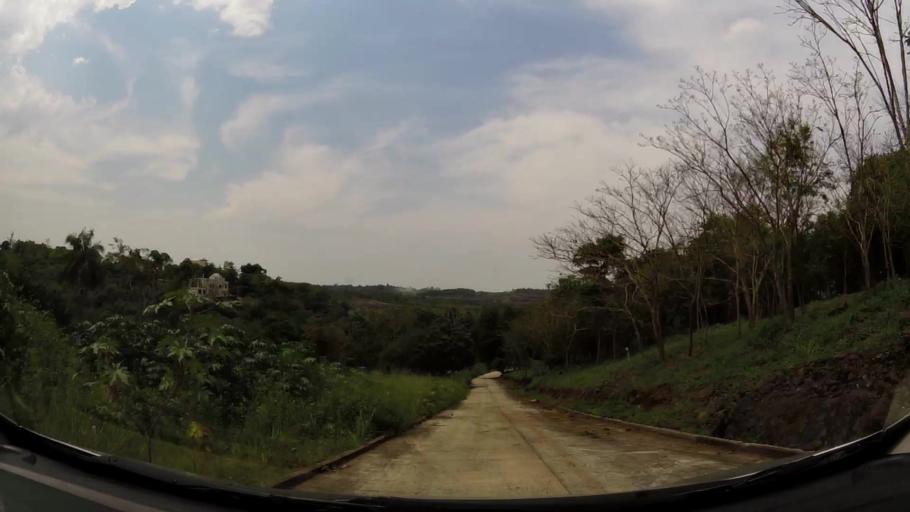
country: PY
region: Alto Parana
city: Ciudad del Este
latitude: -25.4887
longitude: -54.6068
